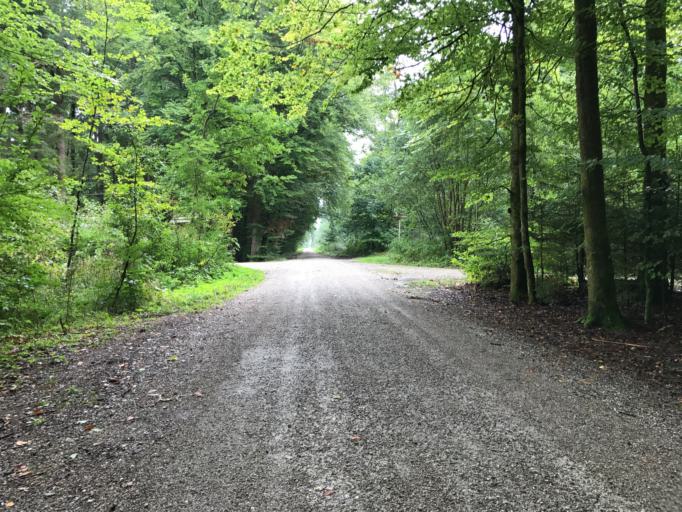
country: DE
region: Bavaria
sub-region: Upper Bavaria
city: Grunwald
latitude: 48.0242
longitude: 11.5297
